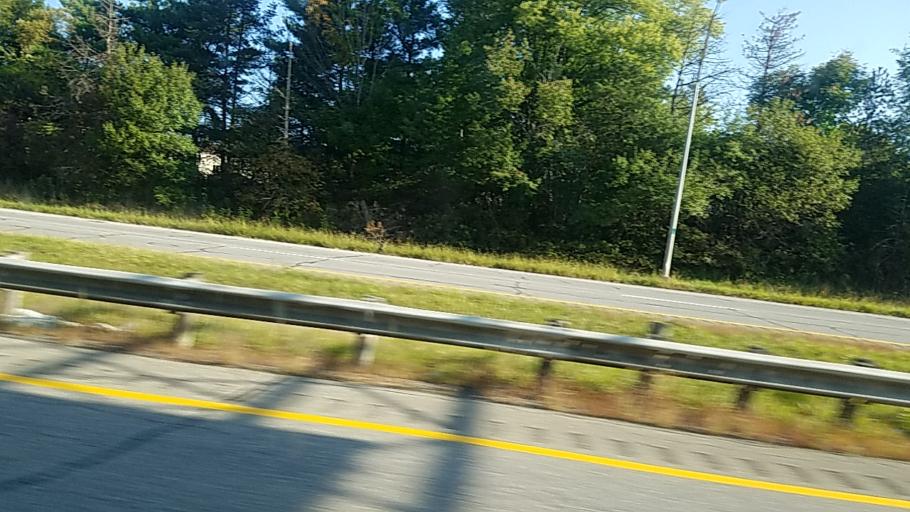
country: US
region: Ohio
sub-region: Trumbull County
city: Girard
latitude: 41.1196
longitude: -80.6988
